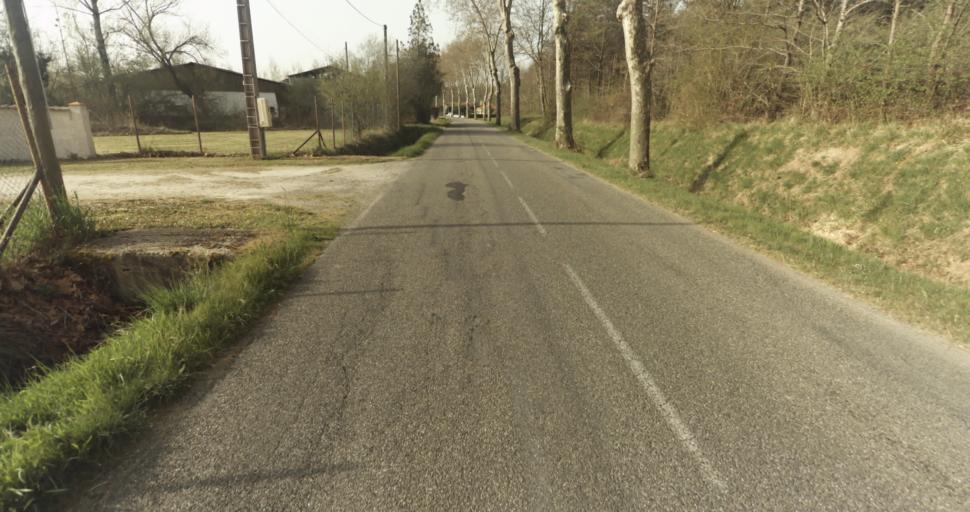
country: FR
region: Midi-Pyrenees
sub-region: Departement du Tarn-et-Garonne
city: Moissac
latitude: 44.1463
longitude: 1.1051
